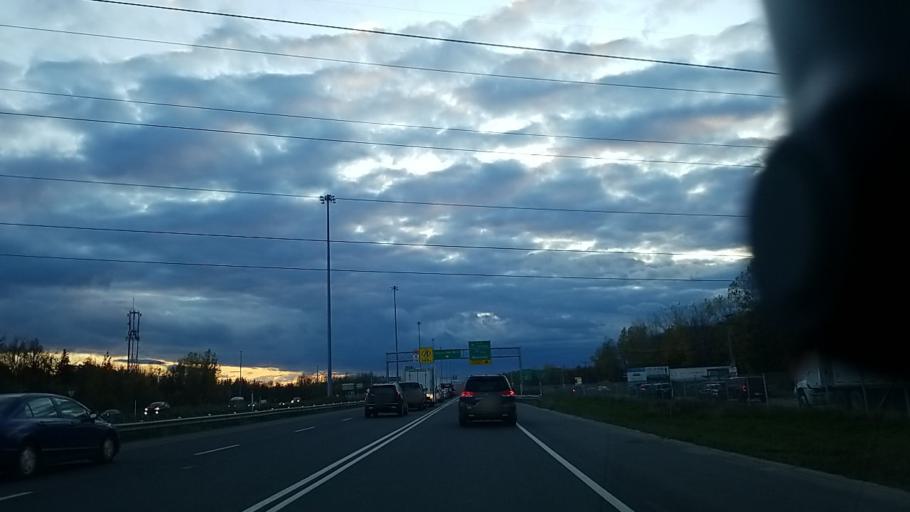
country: CA
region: Quebec
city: Dollard-Des Ormeaux
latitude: 45.5569
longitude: -73.8017
